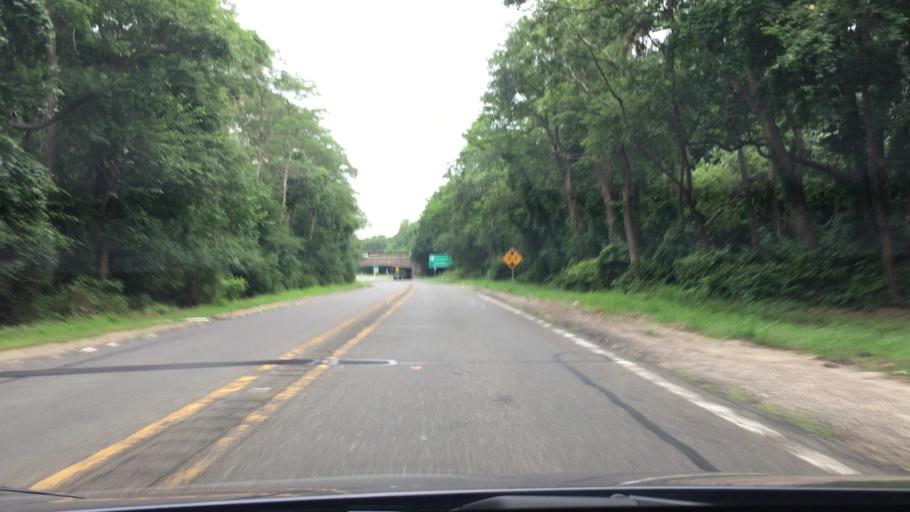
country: US
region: New York
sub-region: Nassau County
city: Plainedge
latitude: 40.7295
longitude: -73.4694
